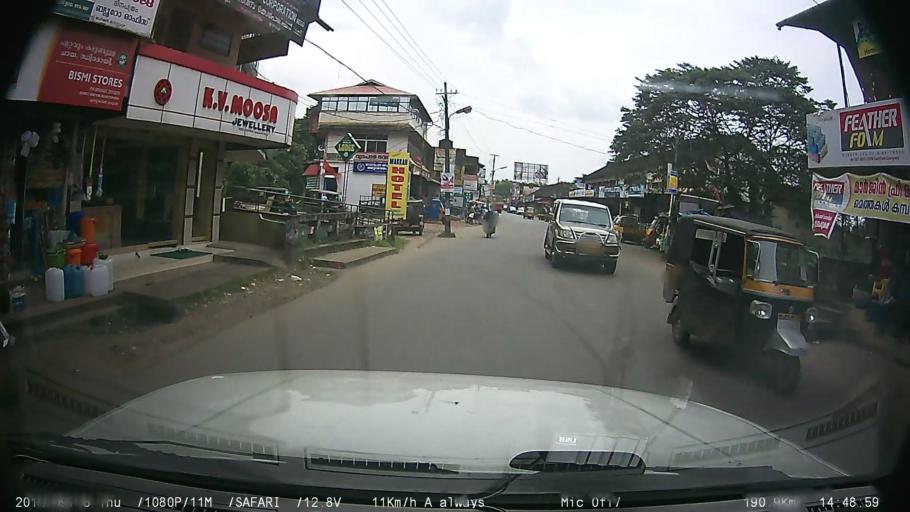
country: IN
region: Kerala
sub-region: Ernakulam
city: Muvattupula
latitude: 9.9892
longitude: 76.5817
